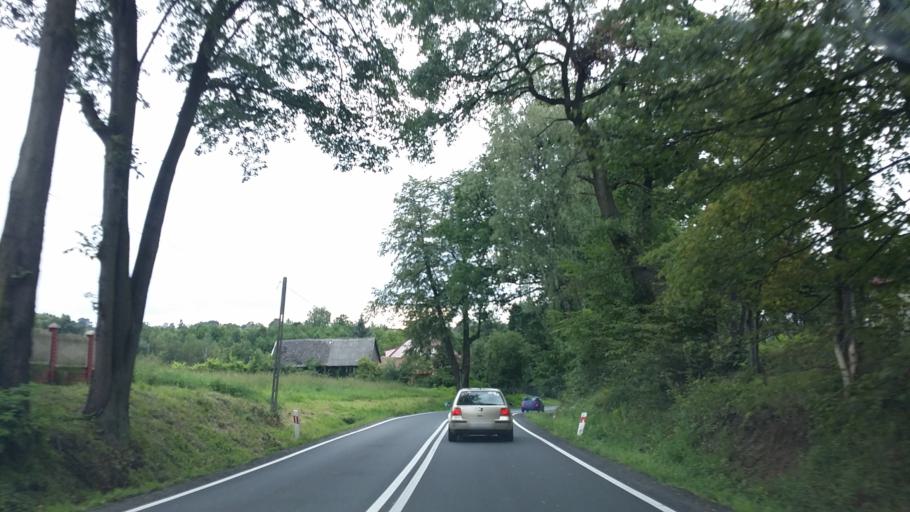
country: PL
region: Lesser Poland Voivodeship
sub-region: Powiat krakowski
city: Czernichow
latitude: 49.9600
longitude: 19.6621
